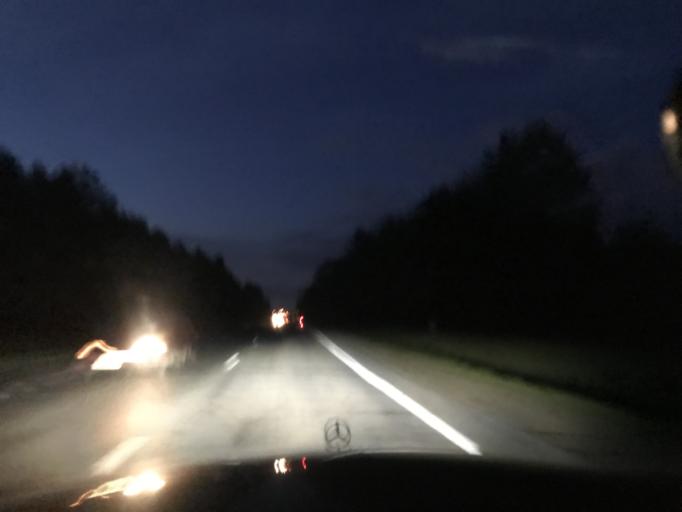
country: BY
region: Brest
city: Brest
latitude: 52.0321
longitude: 23.7292
